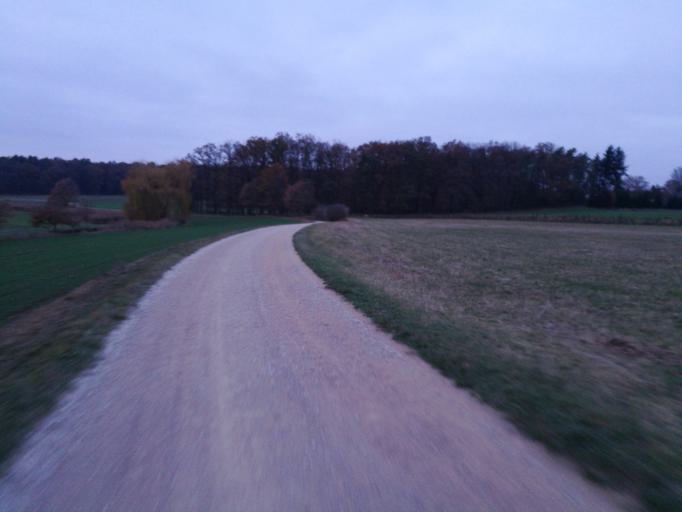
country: DE
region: Bavaria
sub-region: Regierungsbezirk Mittelfranken
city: Obermichelbach
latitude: 49.5085
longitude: 10.9261
